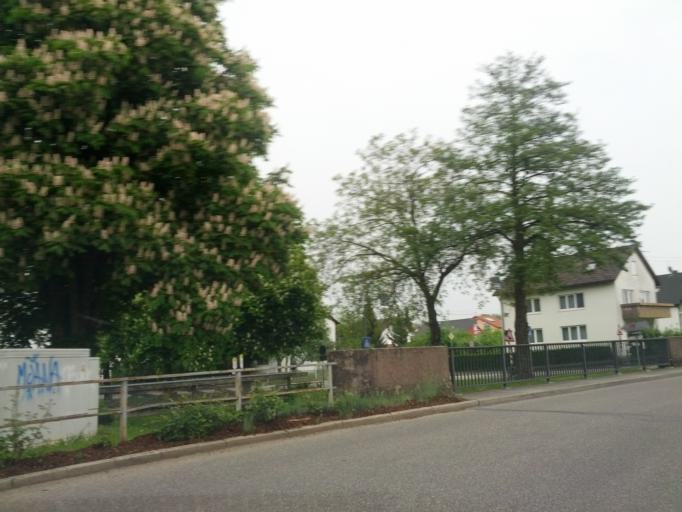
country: DE
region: Baden-Wuerttemberg
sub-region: Freiburg Region
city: Gottenheim
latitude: 48.0509
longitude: 7.7313
